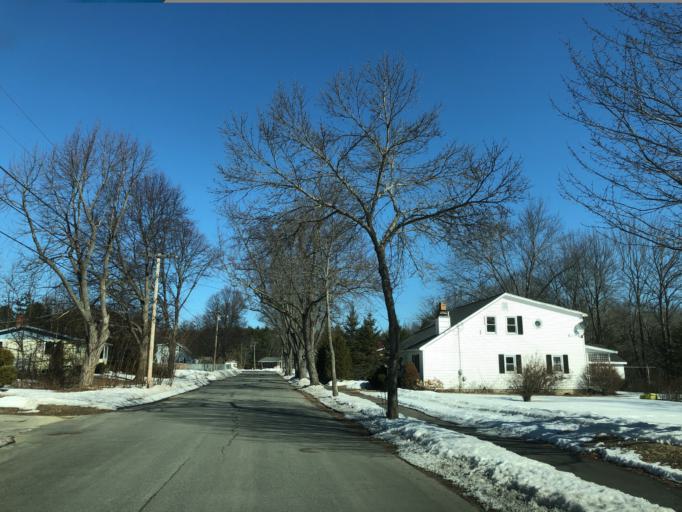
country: US
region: Maine
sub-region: Penobscot County
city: Brewer
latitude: 44.8195
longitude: -68.7536
